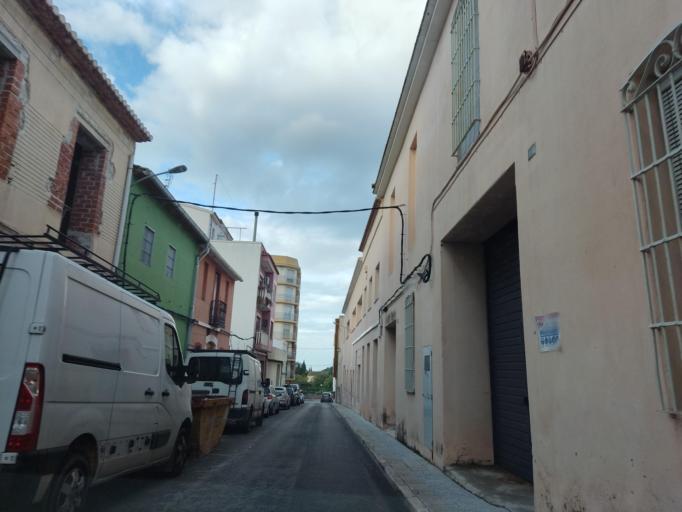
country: ES
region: Valencia
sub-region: Provincia de Alicante
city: Pedreguer
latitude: 38.7956
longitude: 0.0334
